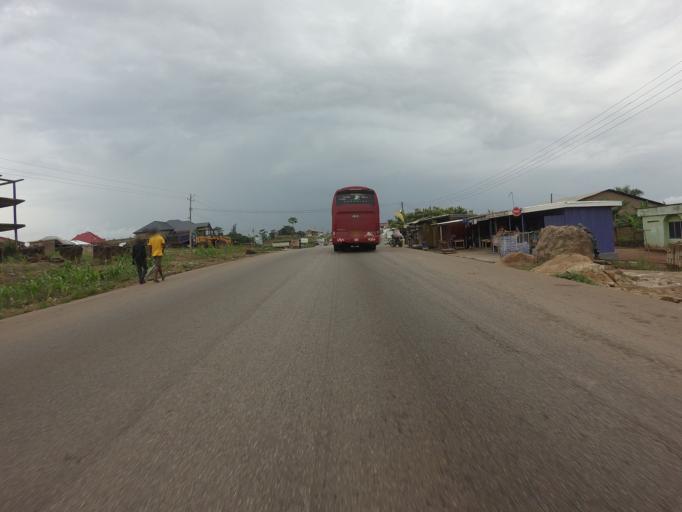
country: GH
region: Ashanti
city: Konongo
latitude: 6.6196
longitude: -1.1932
